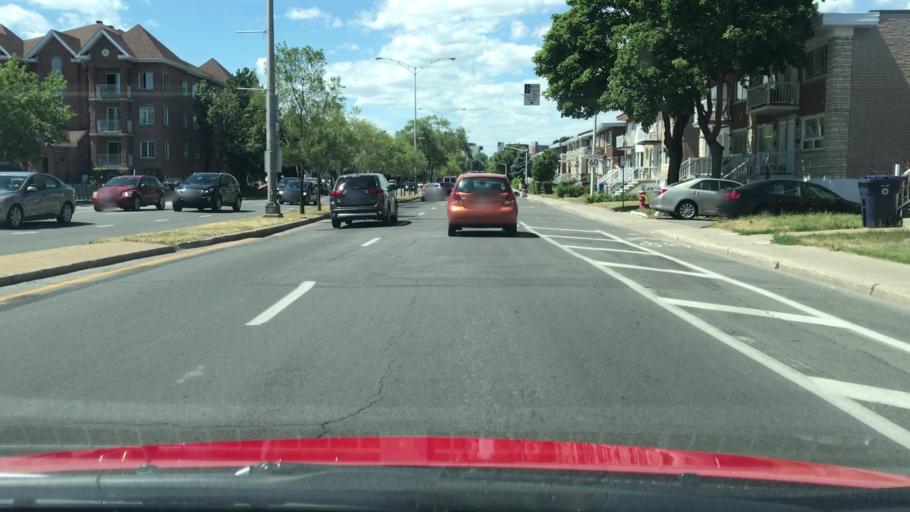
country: CA
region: Quebec
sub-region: Laval
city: Laval
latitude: 45.5397
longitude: -73.7345
